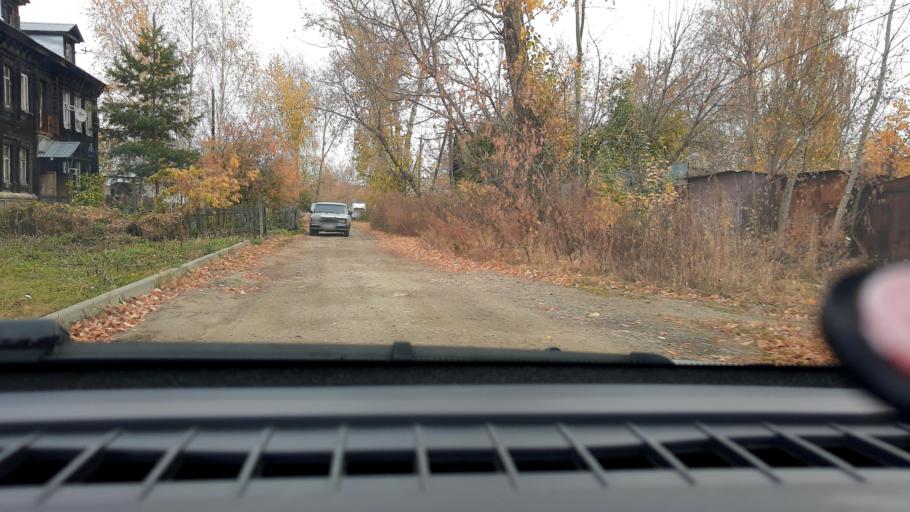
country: RU
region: Nizjnij Novgorod
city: Nizhniy Novgorod
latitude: 56.3156
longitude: 43.9330
